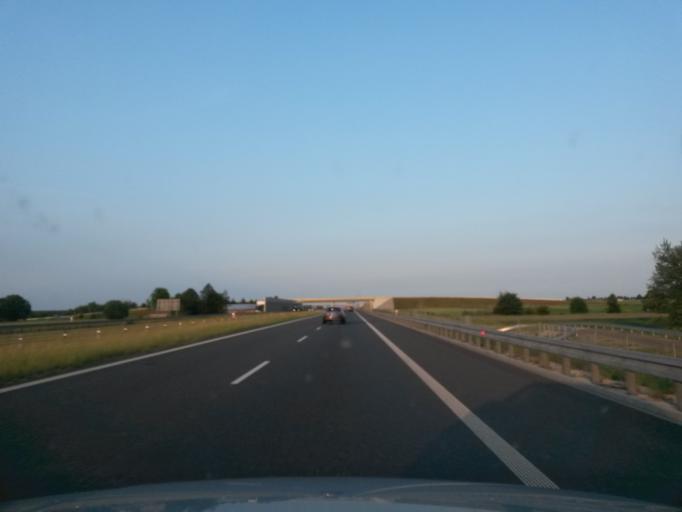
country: PL
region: Lodz Voivodeship
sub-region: Powiat wieruszowski
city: Walichnowy
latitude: 51.3180
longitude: 18.3625
